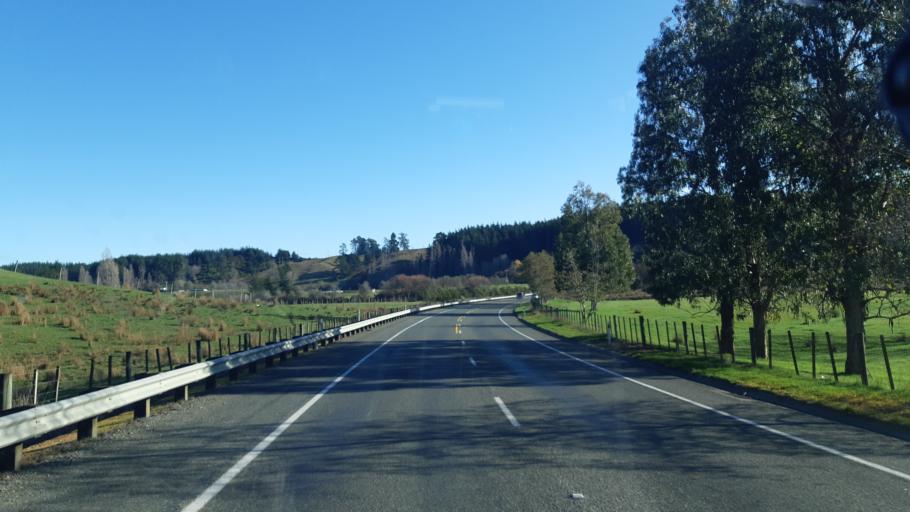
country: NZ
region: Tasman
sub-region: Tasman District
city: Mapua
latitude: -41.2820
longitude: 173.0724
